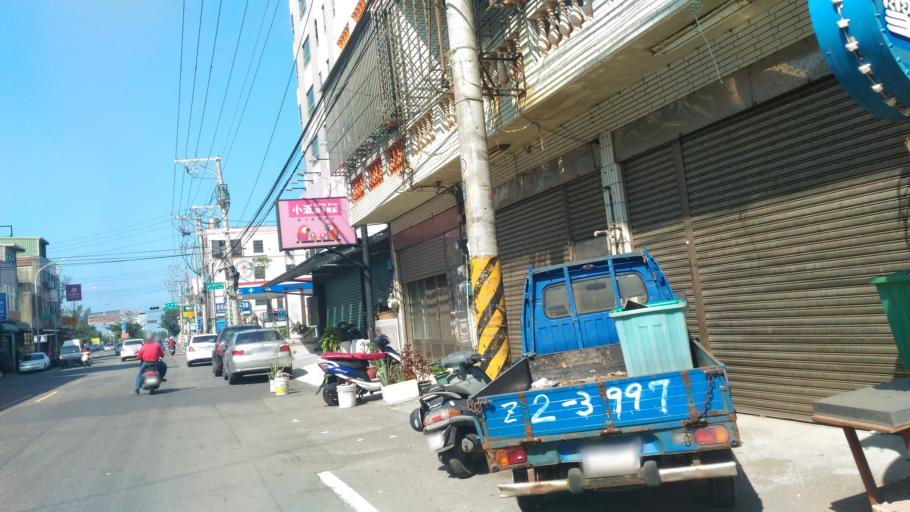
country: TW
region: Taiwan
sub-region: Hsinchu
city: Hsinchu
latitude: 24.8452
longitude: 120.9286
